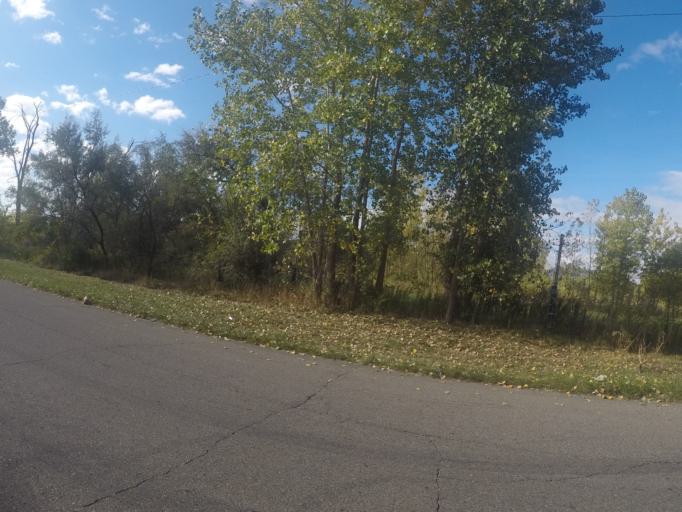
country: US
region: Michigan
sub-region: Wayne County
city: Dearborn
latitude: 42.3562
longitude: -83.1328
